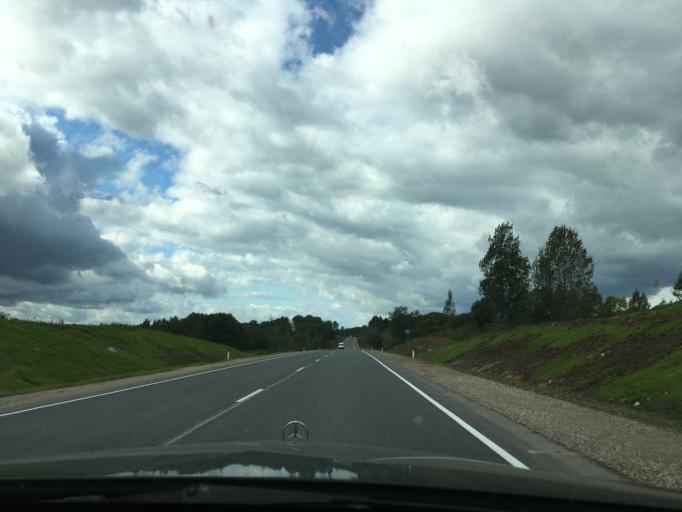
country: RU
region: Pskov
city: Velikiye Luki
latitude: 56.2994
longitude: 31.0579
